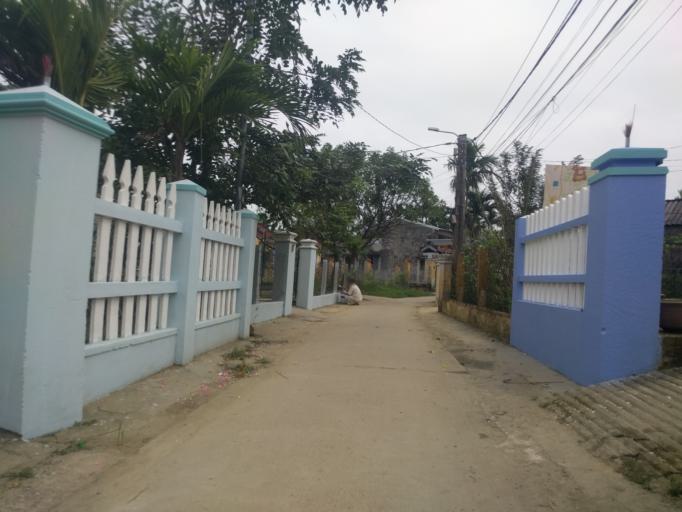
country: VN
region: Quang Nam
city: Hoi An
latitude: 15.8694
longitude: 108.3520
